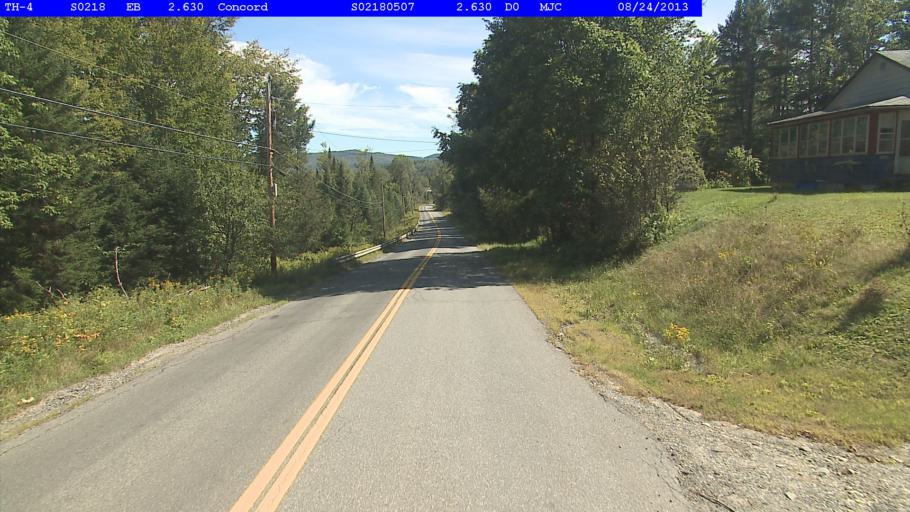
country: US
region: New Hampshire
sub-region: Grafton County
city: Littleton
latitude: 44.4308
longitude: -71.7537
